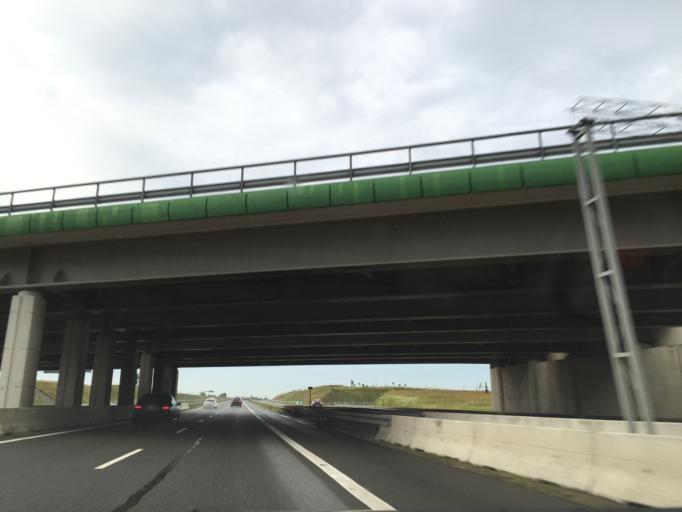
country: PL
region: Podlasie
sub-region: Powiat zambrowski
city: Zambrow
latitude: 52.9796
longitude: 22.2125
